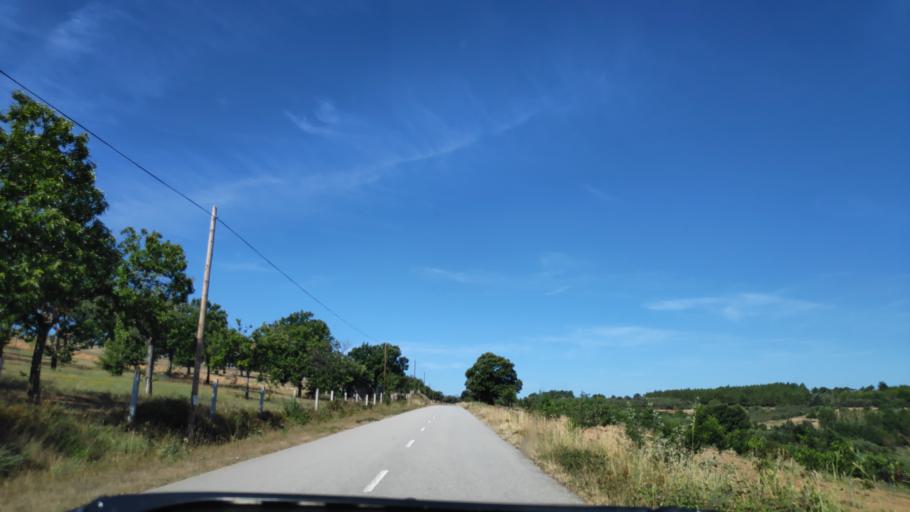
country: ES
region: Castille and Leon
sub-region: Provincia de Zamora
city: Alcanices
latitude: 41.6509
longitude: -6.3760
